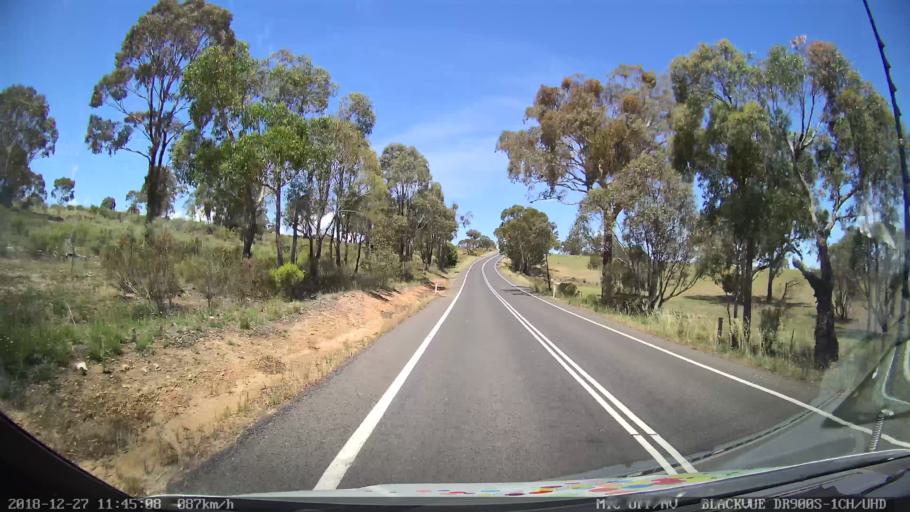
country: AU
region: New South Wales
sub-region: Bathurst Regional
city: Perthville
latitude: -33.5798
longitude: 149.4734
